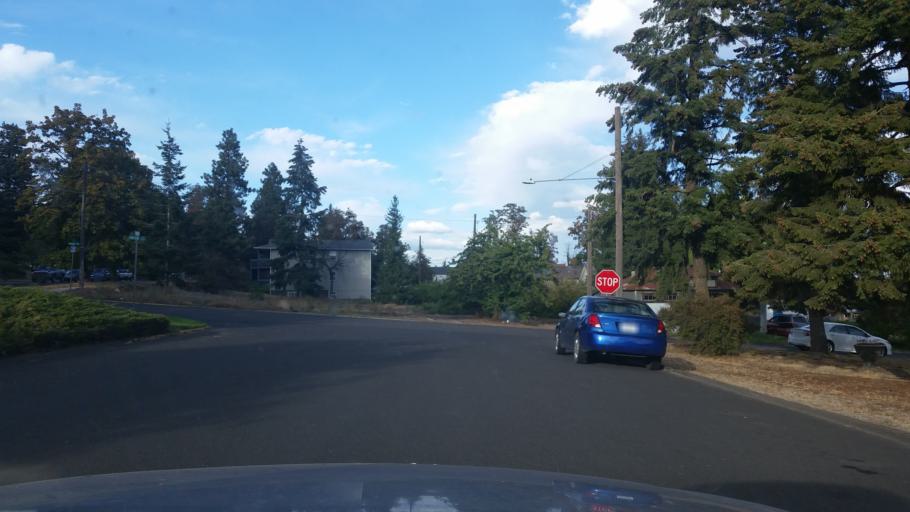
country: US
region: Washington
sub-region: Spokane County
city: Cheney
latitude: 47.4856
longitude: -117.5828
